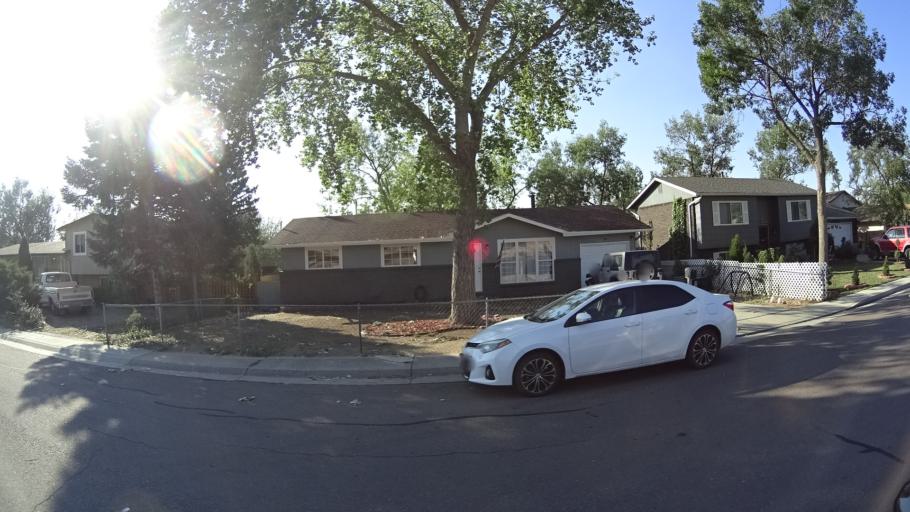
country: US
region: Colorado
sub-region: El Paso County
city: Stratmoor
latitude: 38.7764
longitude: -104.7949
